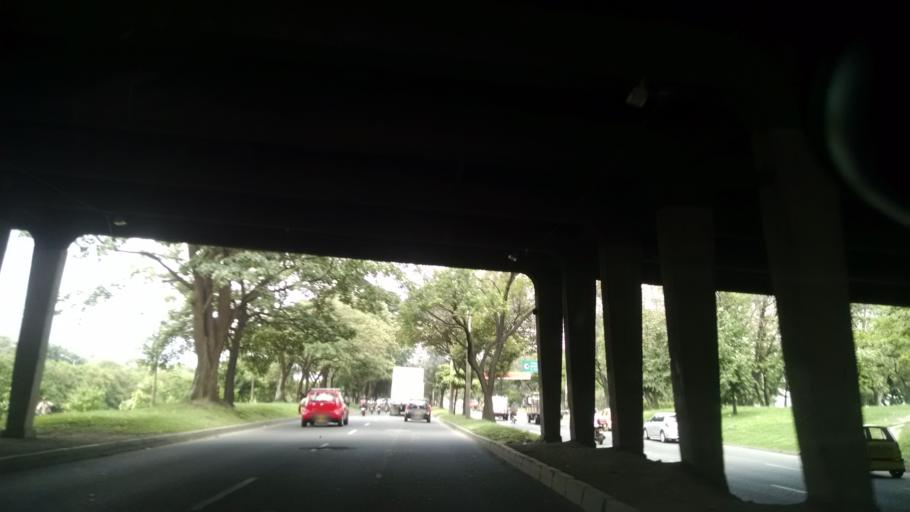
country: CO
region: Antioquia
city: Medellin
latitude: 6.2540
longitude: -75.5769
